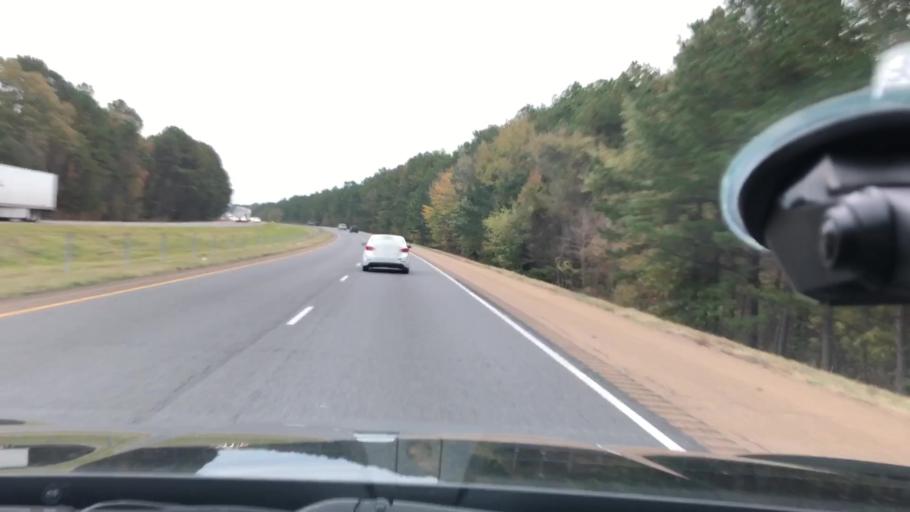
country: US
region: Arkansas
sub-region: Clark County
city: Gurdon
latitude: 33.9572
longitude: -93.2234
